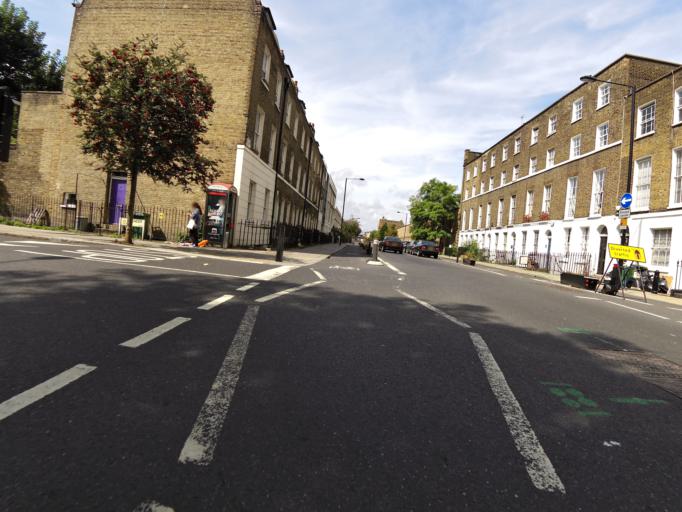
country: GB
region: England
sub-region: Greater London
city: Camden Town
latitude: 51.5374
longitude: -0.1348
